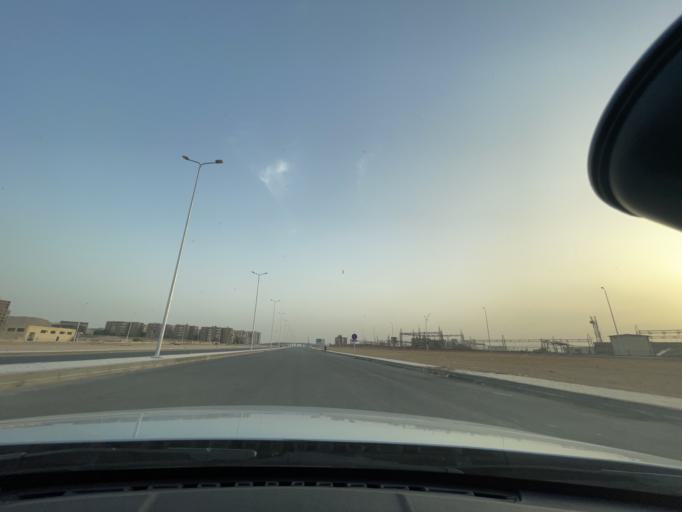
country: EG
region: Muhafazat al Qahirah
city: Cairo
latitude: 30.0421
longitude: 31.3606
